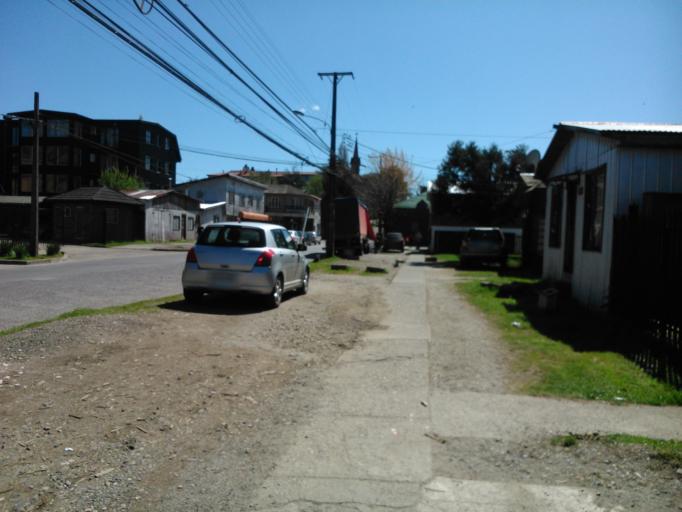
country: CL
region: Los Rios
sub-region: Provincia de Valdivia
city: Valdivia
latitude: -39.8197
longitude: -73.2477
